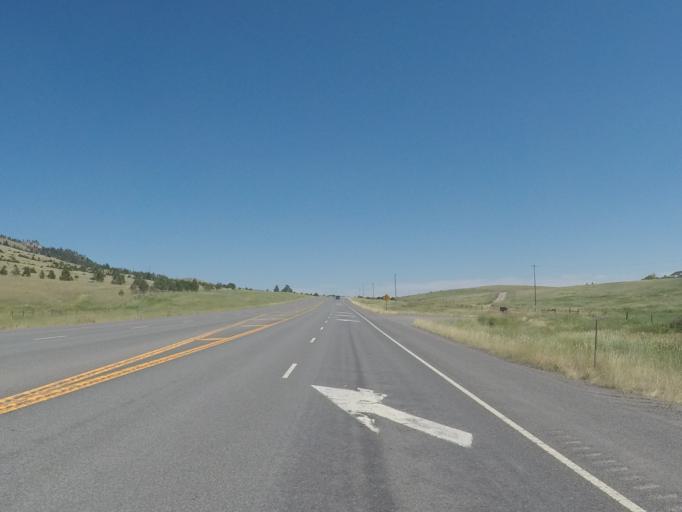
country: US
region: Montana
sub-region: Lewis and Clark County
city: East Helena
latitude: 46.5363
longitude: -111.7283
